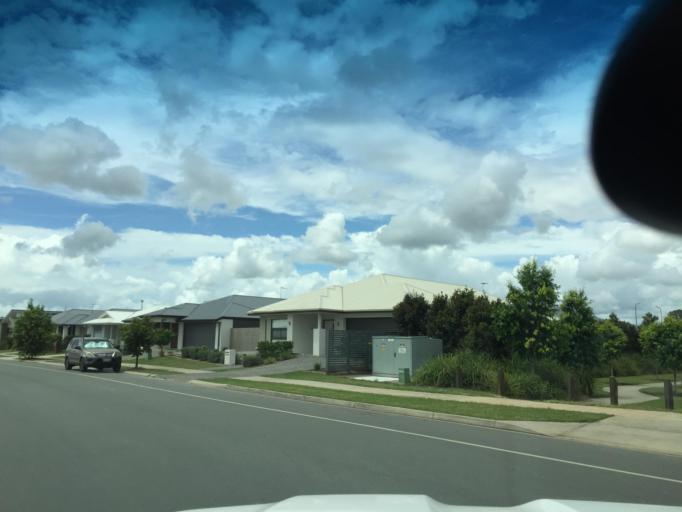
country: AU
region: Queensland
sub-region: Moreton Bay
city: Caboolture South
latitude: -27.0968
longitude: 152.9590
